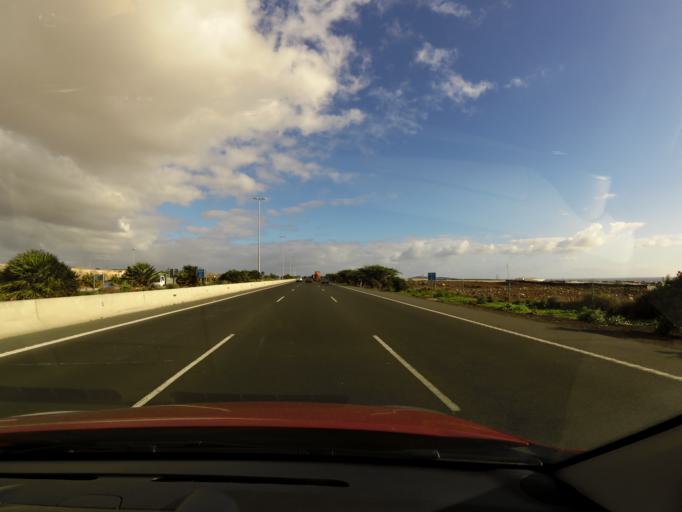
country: ES
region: Canary Islands
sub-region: Provincia de Las Palmas
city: Cruce de Arinaga
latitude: 27.8996
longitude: -15.4038
